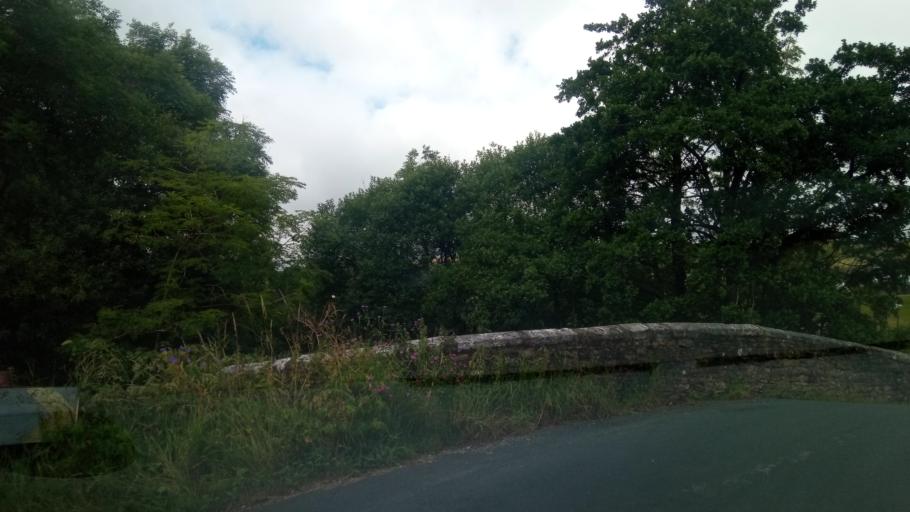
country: GB
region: England
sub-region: North Yorkshire
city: Ingleton
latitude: 54.2768
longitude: -2.3688
